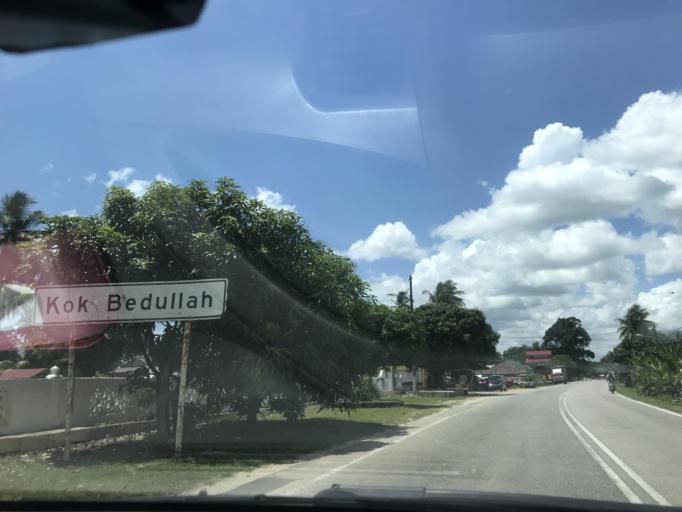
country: MY
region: Kelantan
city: Tumpat
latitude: 6.1990
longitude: 102.1293
